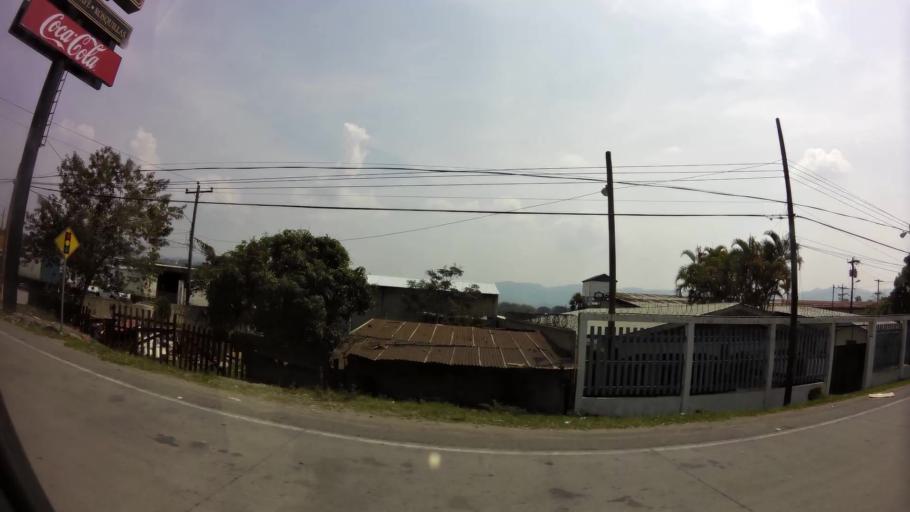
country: HN
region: Comayagua
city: Siguatepeque
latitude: 14.5854
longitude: -87.8497
